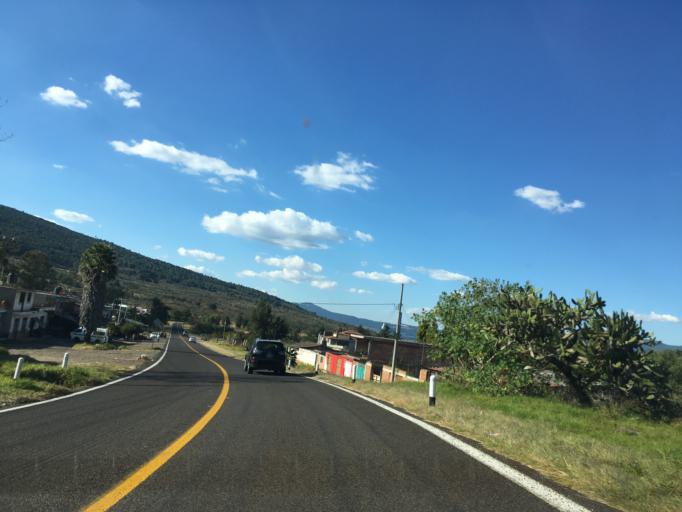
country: MX
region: Michoacan
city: Tzintzuntzan
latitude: 19.6035
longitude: -101.5731
